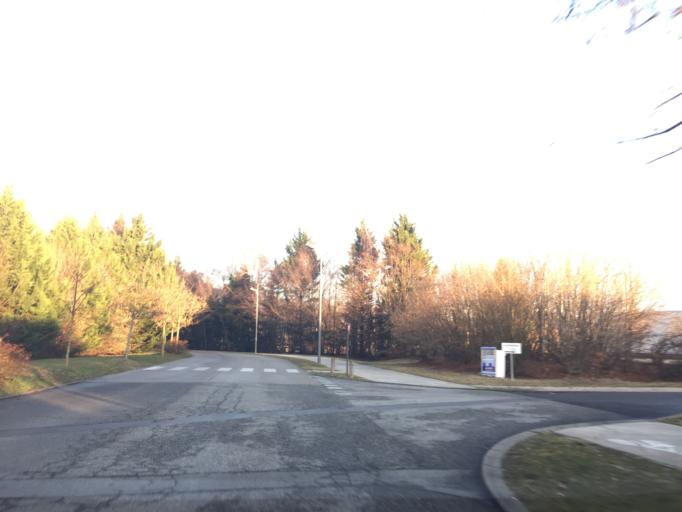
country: FR
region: Rhone-Alpes
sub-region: Departement de la Savoie
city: Le Bourget-du-Lac
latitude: 45.6448
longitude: 5.8732
